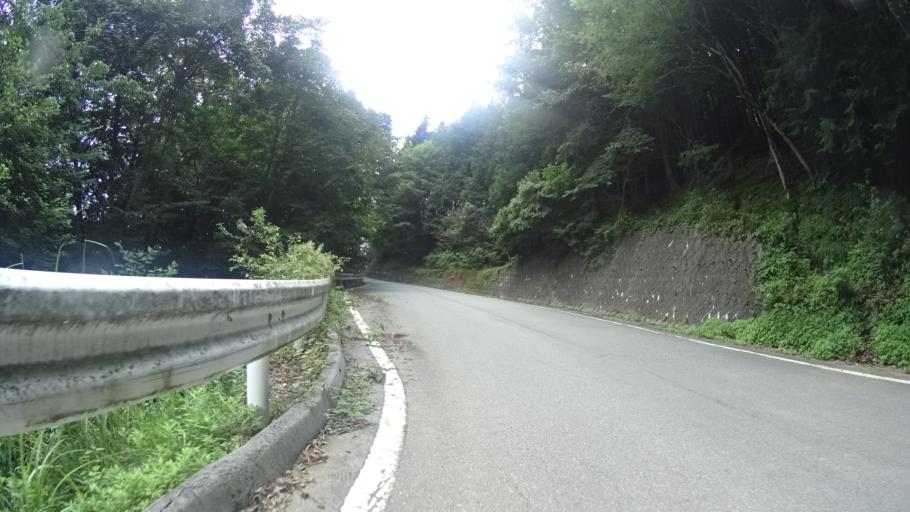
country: JP
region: Yamanashi
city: Enzan
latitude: 35.7982
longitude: 138.6811
